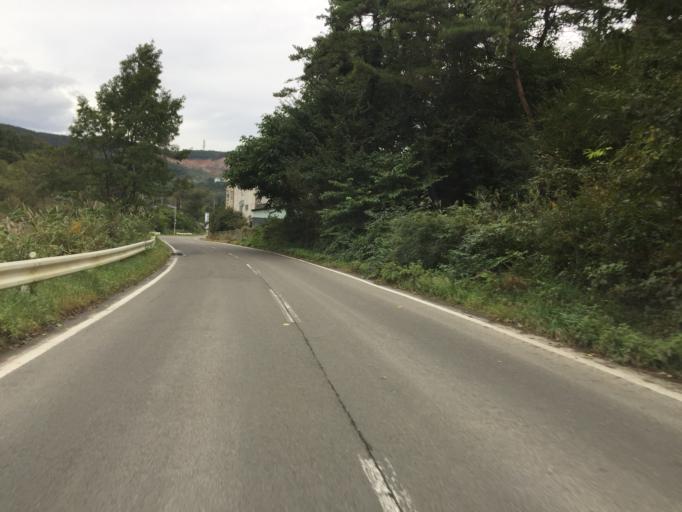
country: JP
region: Miyagi
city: Marumori
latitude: 37.8941
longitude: 140.7169
